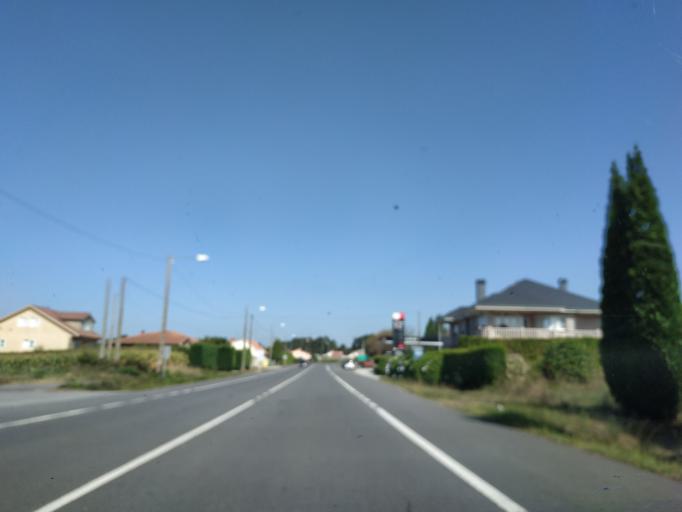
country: ES
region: Galicia
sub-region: Provincia da Coruna
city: Laracha
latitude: 43.2500
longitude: -8.6157
